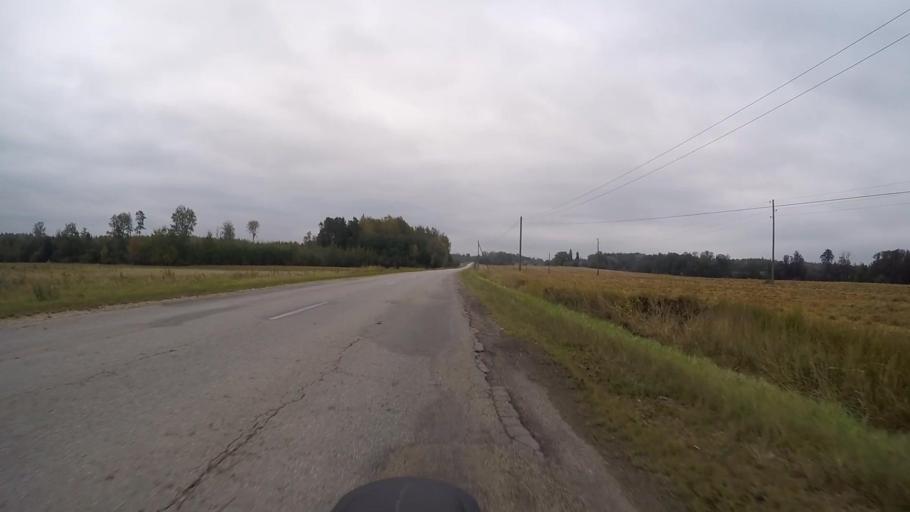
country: LV
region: Seja
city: Loja
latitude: 57.2746
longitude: 24.5621
